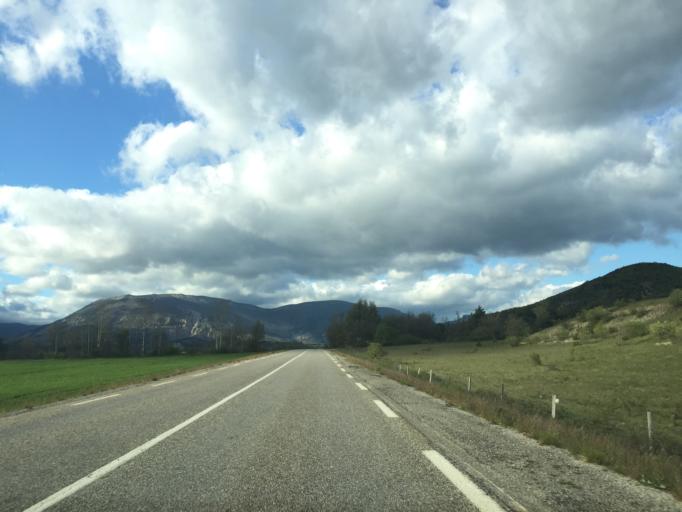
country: FR
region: Provence-Alpes-Cote d'Azur
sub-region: Departement des Hautes-Alpes
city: Serres
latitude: 44.4693
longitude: 5.7252
